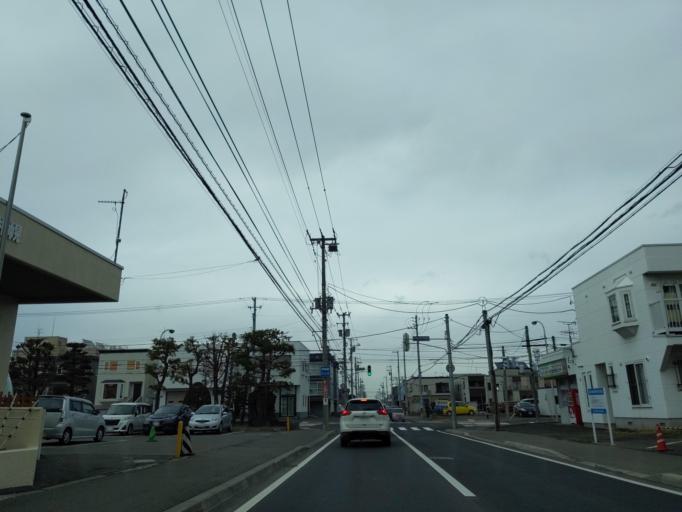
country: JP
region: Hokkaido
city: Sapporo
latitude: 43.0885
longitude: 141.3988
